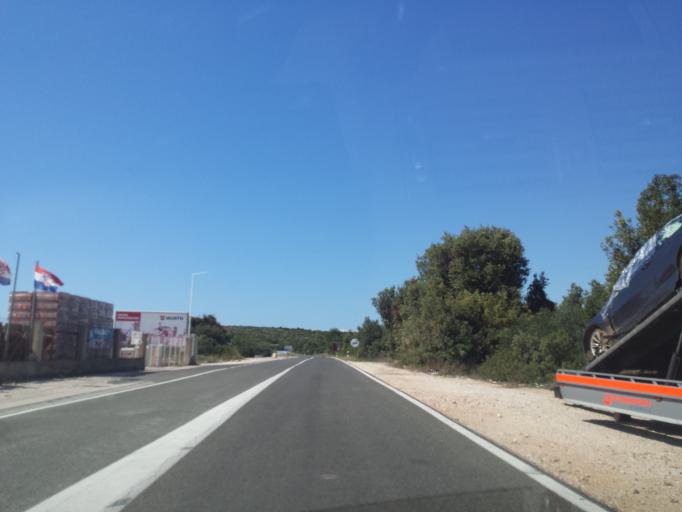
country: HR
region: Sibensko-Kniniska
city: Rogoznica
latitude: 43.5421
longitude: 15.9676
